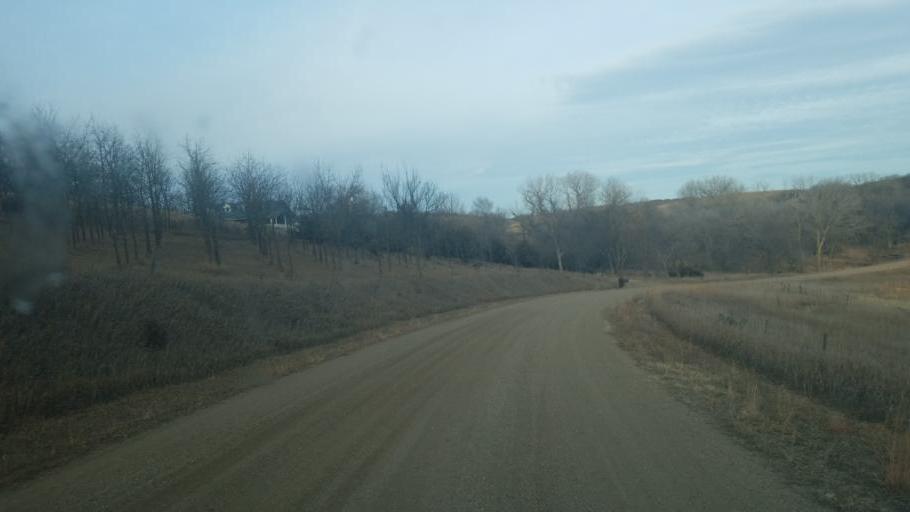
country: US
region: Nebraska
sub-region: Knox County
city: Center
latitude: 42.6904
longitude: -97.8077
